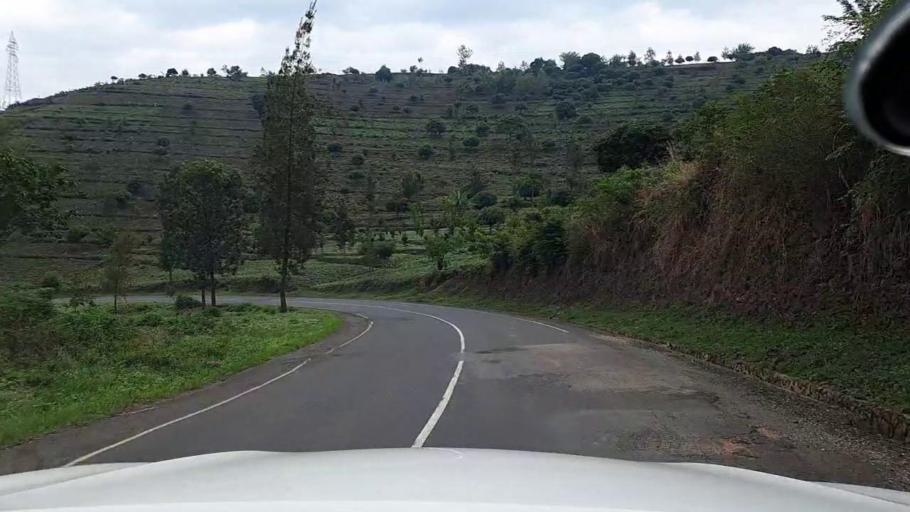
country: RW
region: Western Province
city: Cyangugu
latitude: -2.6739
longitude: 29.0029
